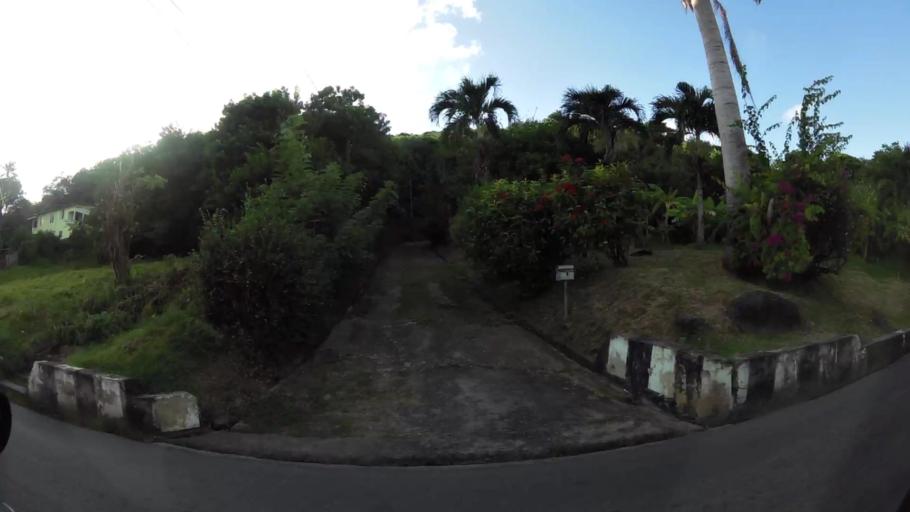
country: TT
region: Tobago
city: Scarborough
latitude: 11.1850
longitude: -60.6984
